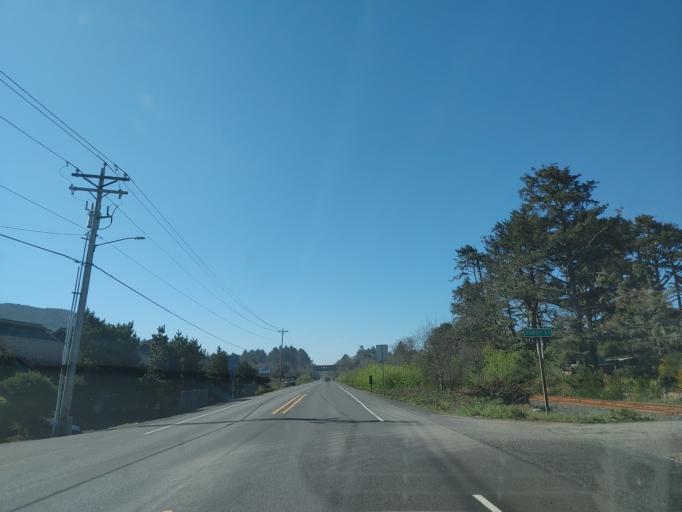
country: US
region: Oregon
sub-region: Tillamook County
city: Rockaway Beach
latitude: 45.5961
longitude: -123.9468
